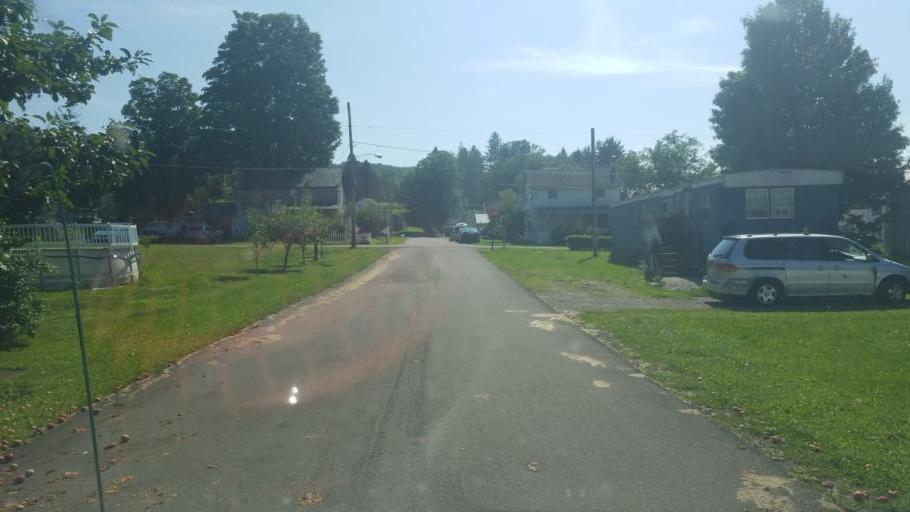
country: US
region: New York
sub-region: Allegany County
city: Bolivar
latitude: 42.0844
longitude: -78.0624
